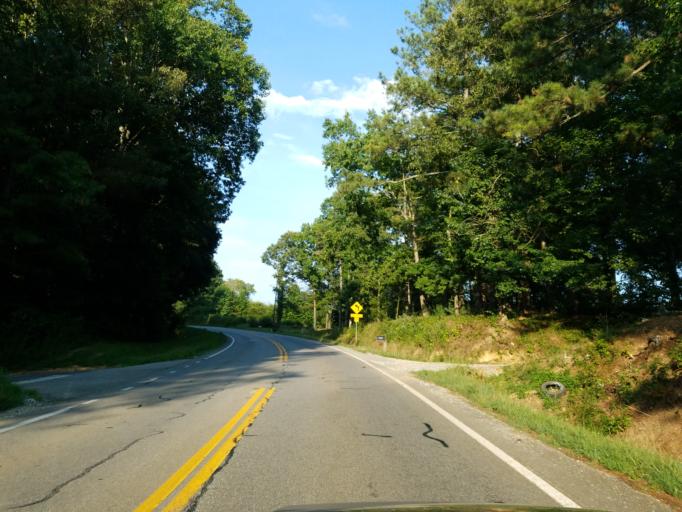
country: US
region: Georgia
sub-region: Pickens County
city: Jasper
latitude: 34.5105
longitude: -84.5481
